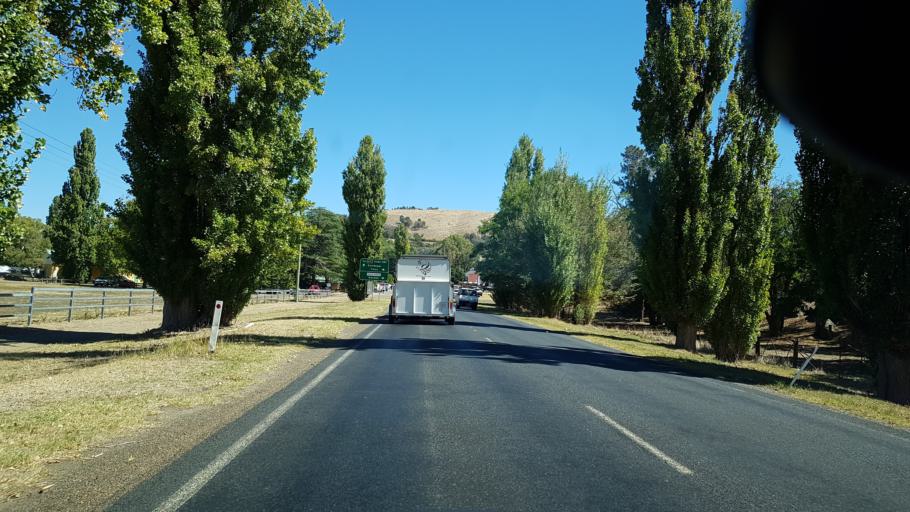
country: AU
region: New South Wales
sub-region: Gundagai
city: Gundagai
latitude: -34.8232
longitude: 148.3282
